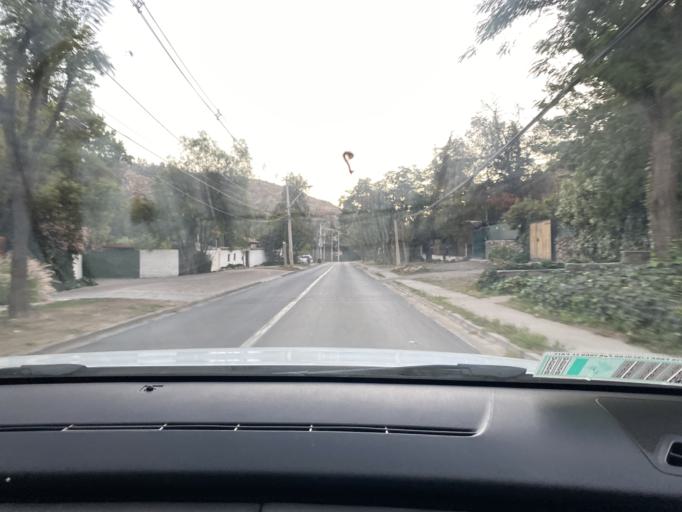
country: CL
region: Santiago Metropolitan
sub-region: Provincia de Santiago
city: Villa Presidente Frei, Nunoa, Santiago, Chile
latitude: -33.3596
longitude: -70.4859
